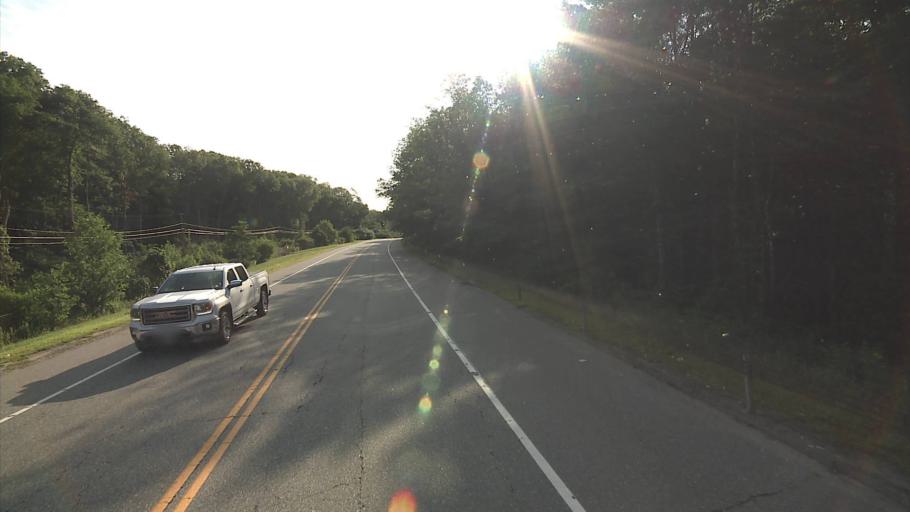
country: US
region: Connecticut
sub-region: New London County
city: Preston City
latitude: 41.4660
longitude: -71.9267
